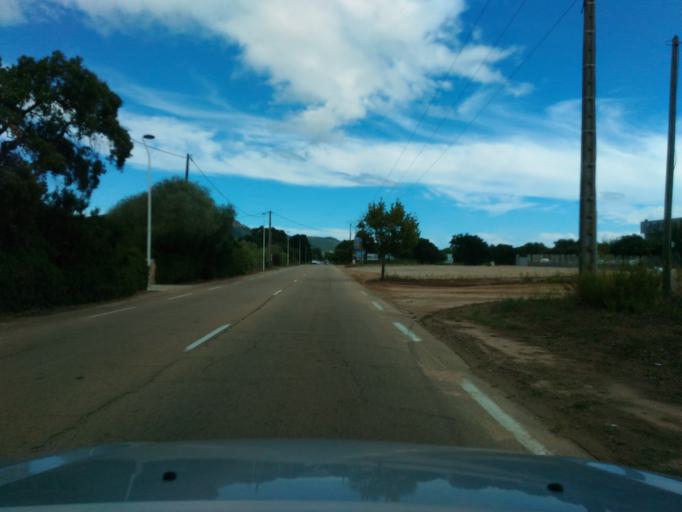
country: FR
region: Corsica
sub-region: Departement de la Corse-du-Sud
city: Porto-Vecchio
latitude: 41.6937
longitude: 9.3359
